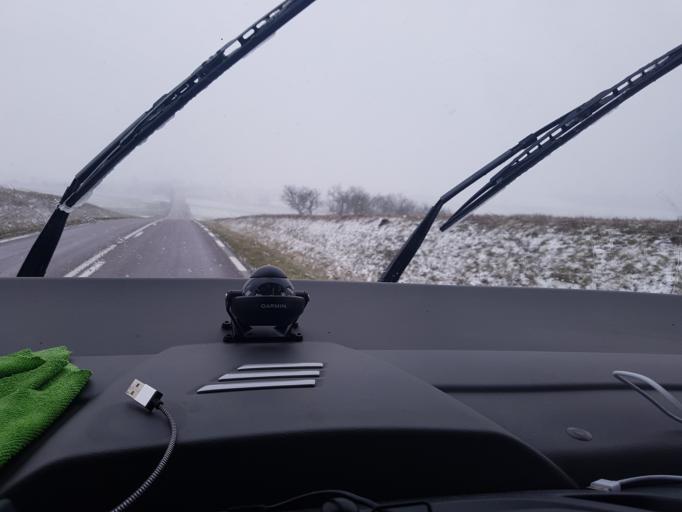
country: FR
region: Lorraine
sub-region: Departement de la Moselle
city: Dieuze
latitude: 48.7265
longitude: 6.7109
